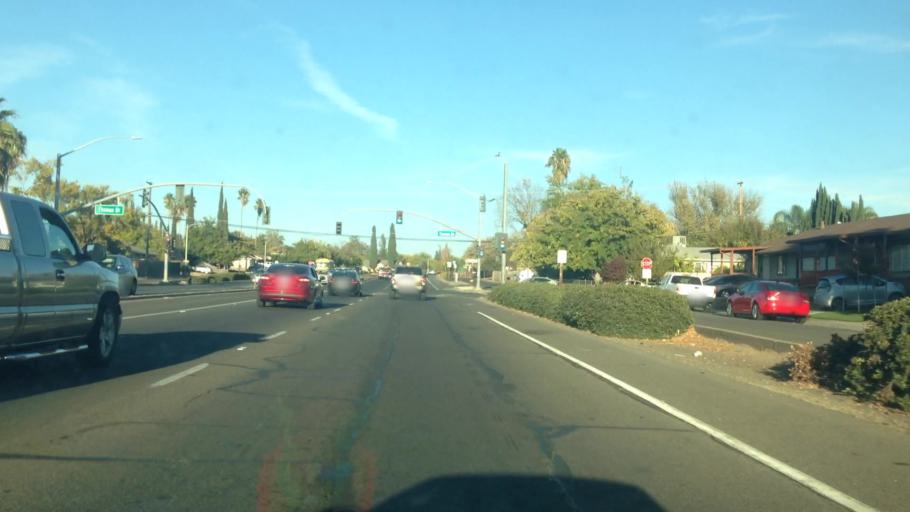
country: US
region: California
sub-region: Sacramento County
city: North Highlands
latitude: 38.6916
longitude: -121.3762
